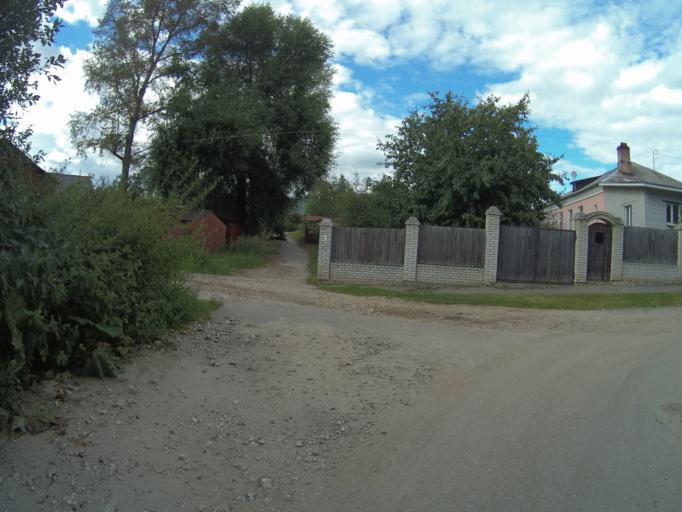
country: RU
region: Vladimir
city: Vladimir
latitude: 56.1208
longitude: 40.3537
